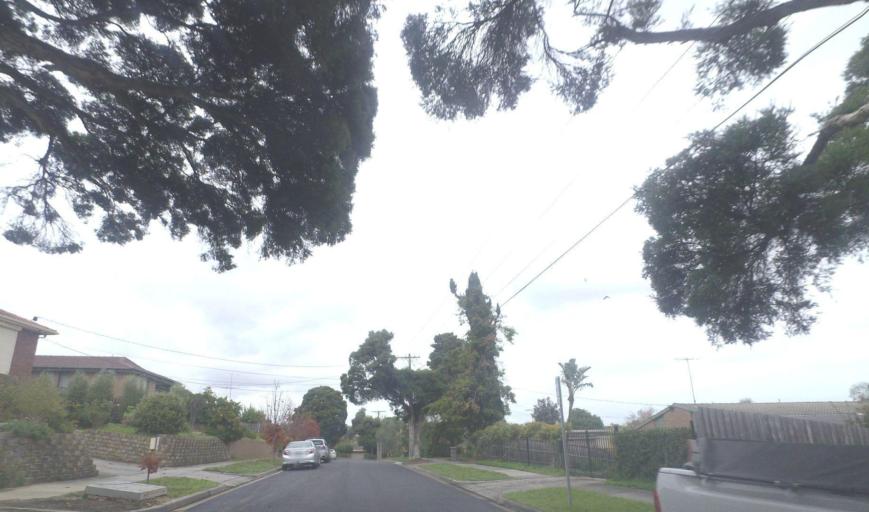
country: AU
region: Victoria
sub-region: Manningham
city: Doncaster
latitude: -37.7835
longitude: 145.1190
